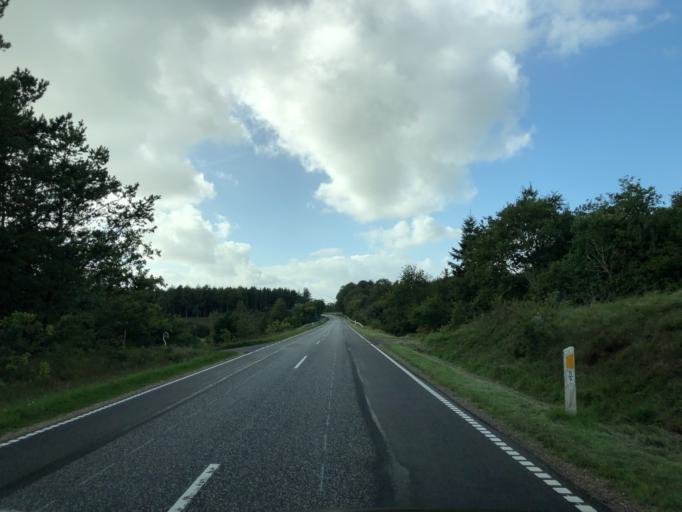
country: DK
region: Central Jutland
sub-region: Holstebro Kommune
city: Holstebro
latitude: 56.3722
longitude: 8.5231
